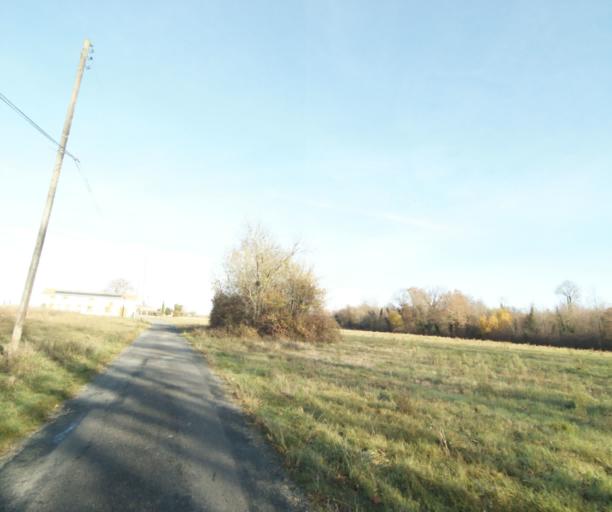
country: FR
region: Poitou-Charentes
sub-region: Departement de la Charente-Maritime
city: Cherac
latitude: 45.7392
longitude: -0.4671
